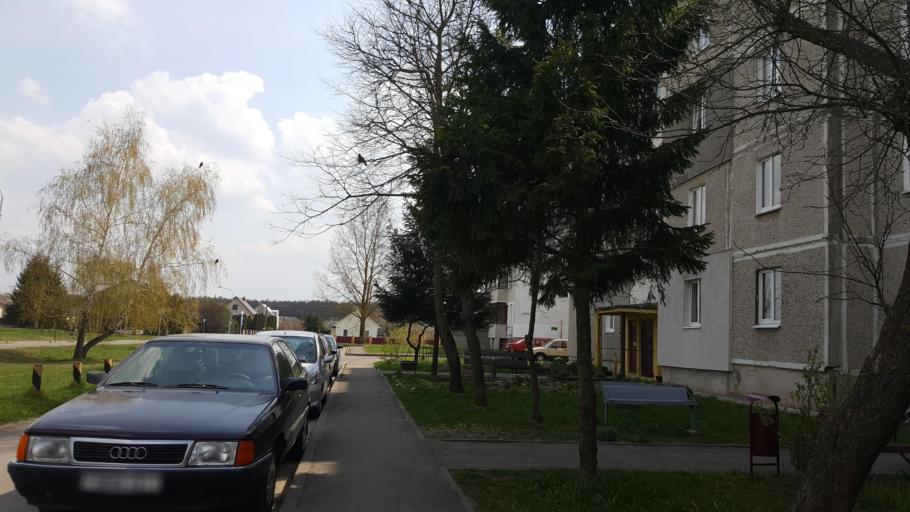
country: BY
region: Brest
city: Zhabinka
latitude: 52.1924
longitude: 24.0340
